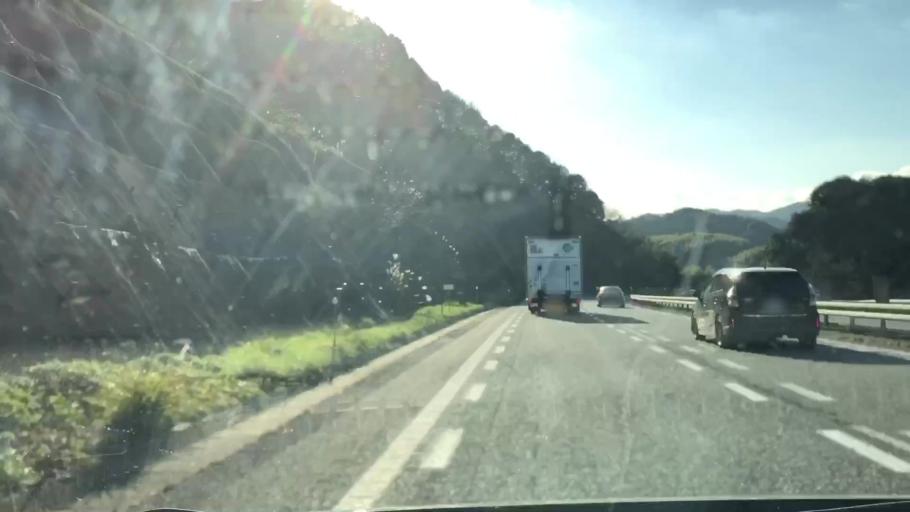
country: JP
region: Yamaguchi
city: Onoda
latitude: 34.1109
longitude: 131.1568
